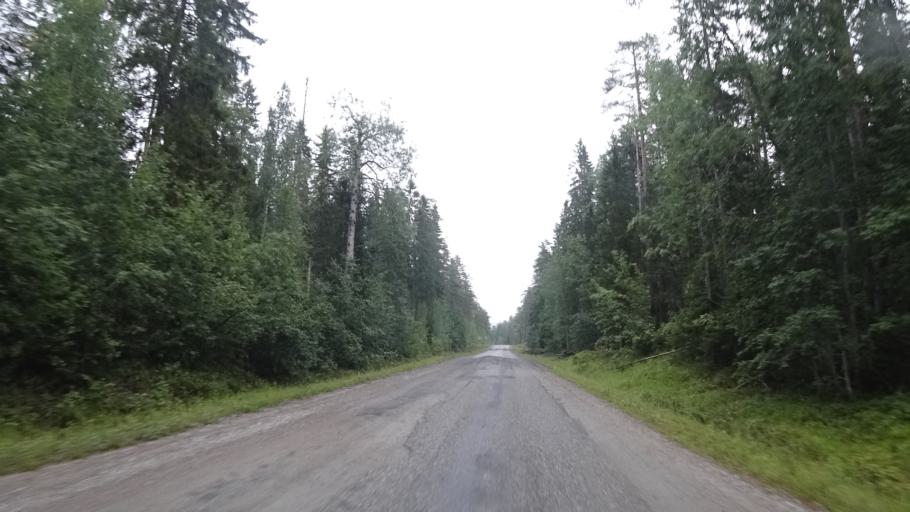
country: FI
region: North Karelia
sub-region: Joensuu
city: Ilomantsi
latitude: 63.2275
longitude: 30.8537
